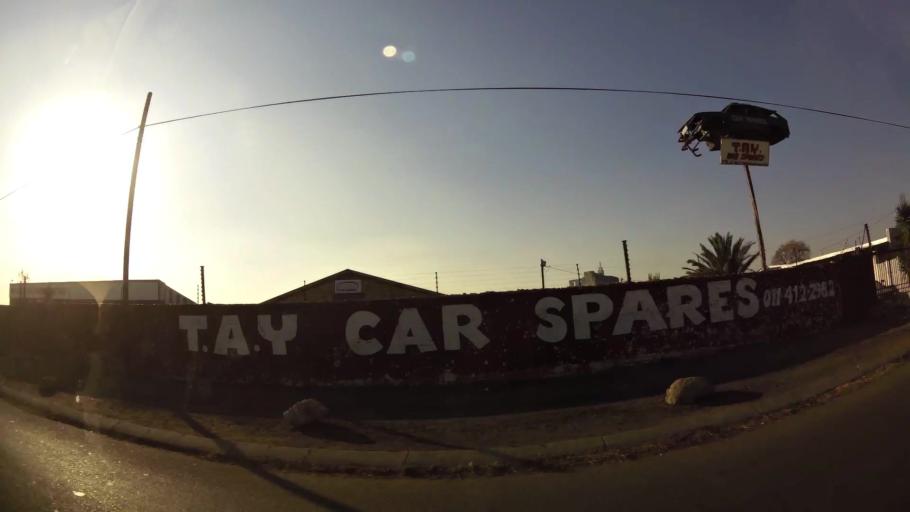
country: ZA
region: Gauteng
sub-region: West Rand District Municipality
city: Randfontein
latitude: -26.1924
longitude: 27.6906
